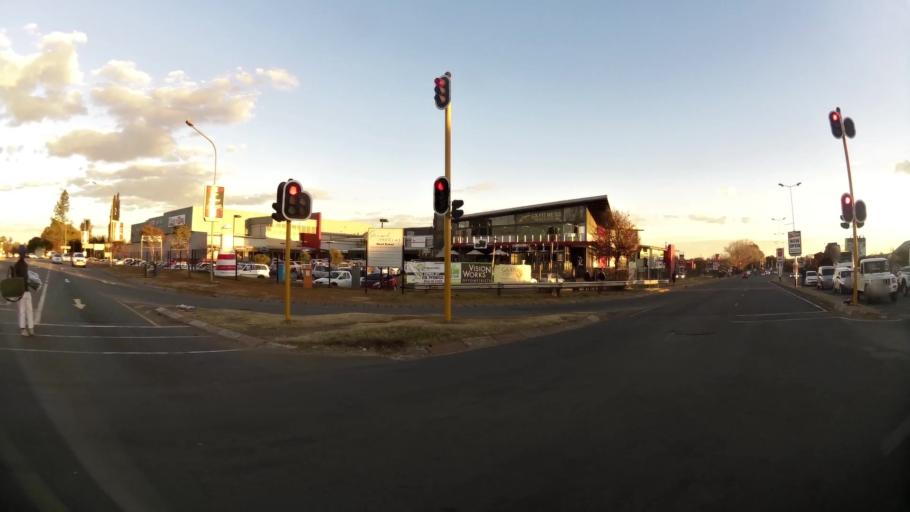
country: ZA
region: North-West
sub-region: Dr Kenneth Kaunda District Municipality
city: Potchefstroom
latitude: -26.7121
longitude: 27.1089
